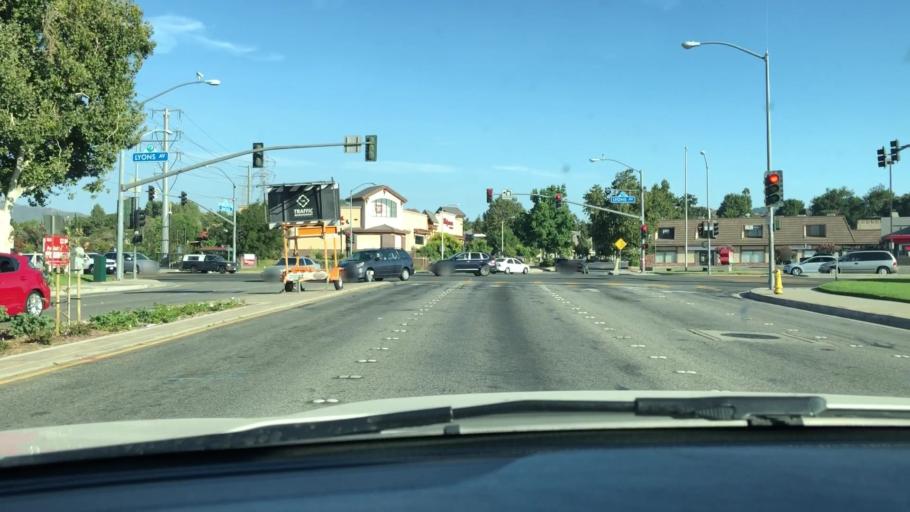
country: US
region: California
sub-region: Los Angeles County
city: Santa Clarita
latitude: 34.3803
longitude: -118.5410
